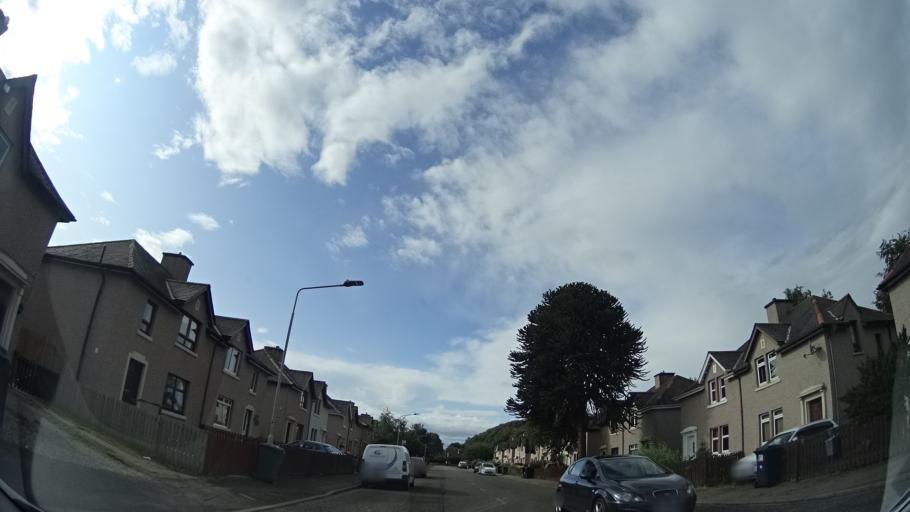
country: GB
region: Scotland
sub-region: Highland
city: Inverness
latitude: 57.4745
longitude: -4.2396
